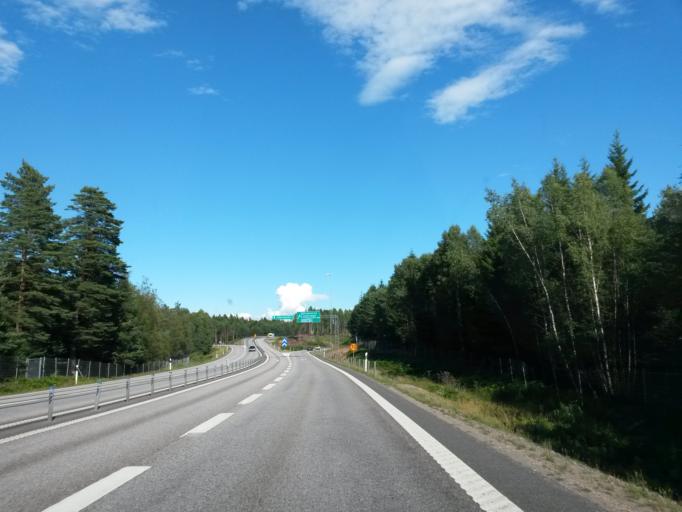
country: SE
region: Vaestra Goetaland
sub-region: Trollhattan
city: Trollhattan
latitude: 58.3347
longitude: 12.2915
